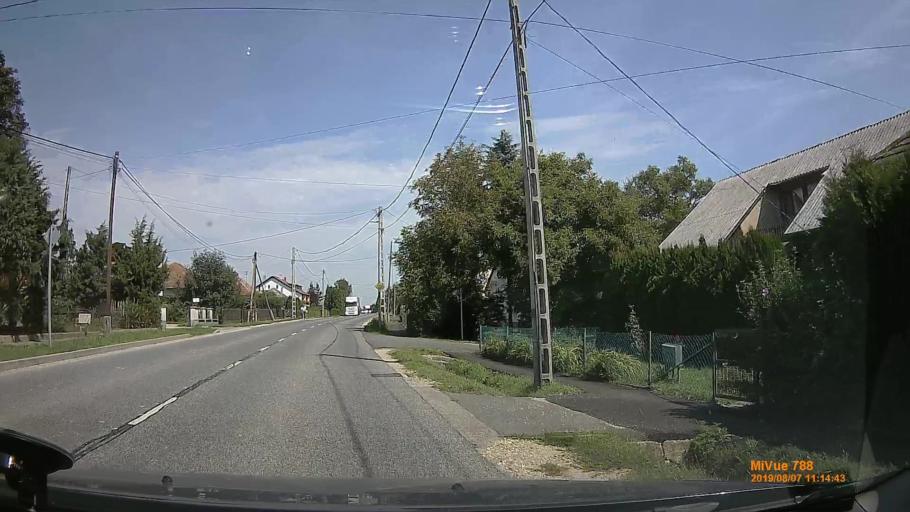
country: HU
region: Zala
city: Lenti
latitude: 46.7088
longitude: 16.5521
